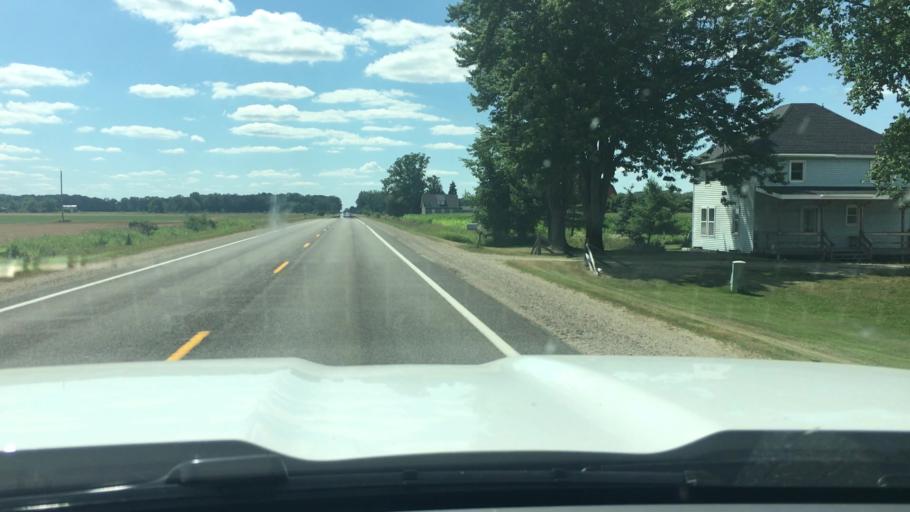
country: US
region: Michigan
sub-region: Clinton County
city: Ovid
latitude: 43.1760
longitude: -84.3760
